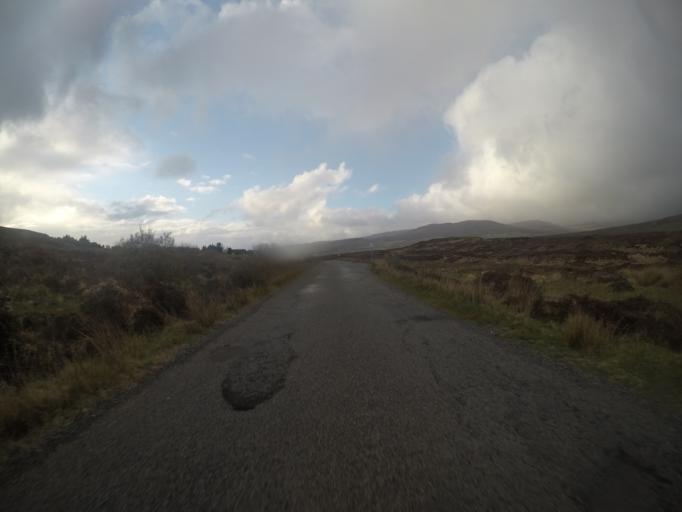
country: GB
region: Scotland
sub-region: Highland
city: Isle of Skye
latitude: 57.4641
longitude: -6.2972
